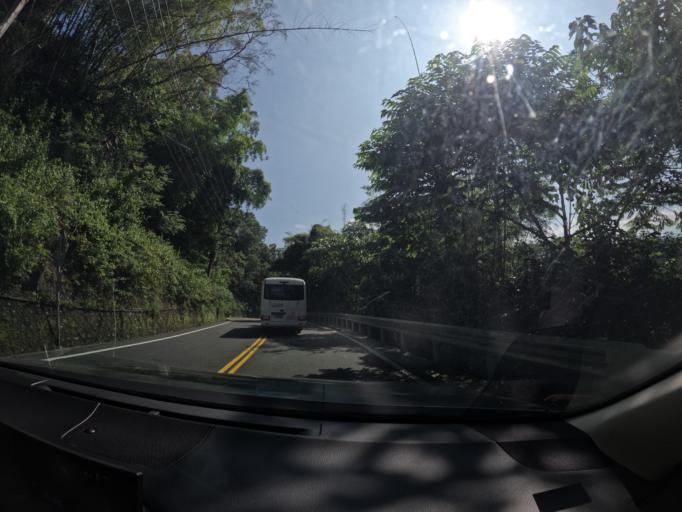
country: TW
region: Taiwan
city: Yujing
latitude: 23.0692
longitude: 120.6473
